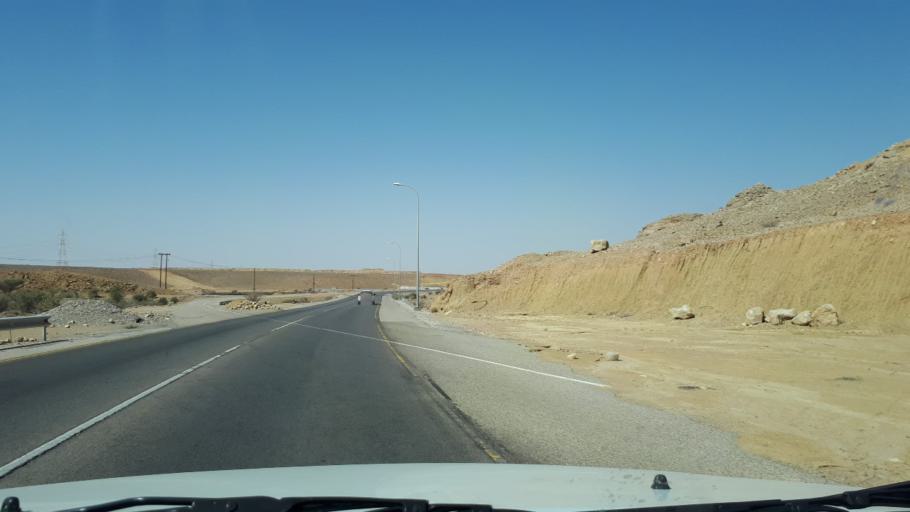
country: OM
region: Ash Sharqiyah
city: Sur
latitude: 22.3175
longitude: 59.3074
